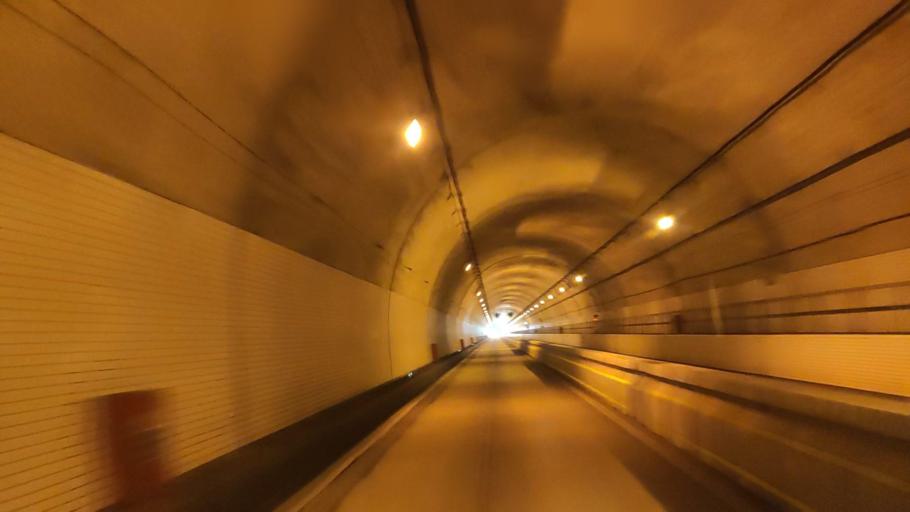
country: JP
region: Toyama
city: Nyuzen
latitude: 36.9639
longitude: 137.5901
